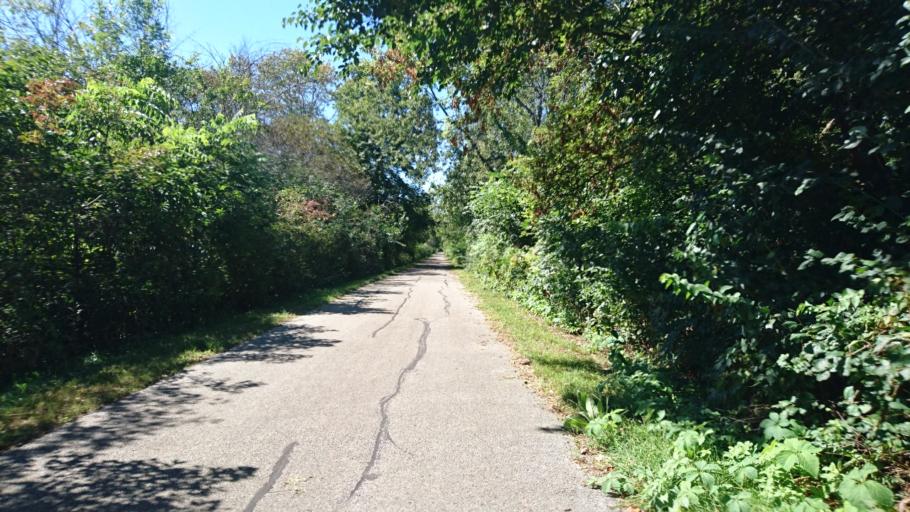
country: US
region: Illinois
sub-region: Cook County
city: Park Forest
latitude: 41.4991
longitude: -87.6820
